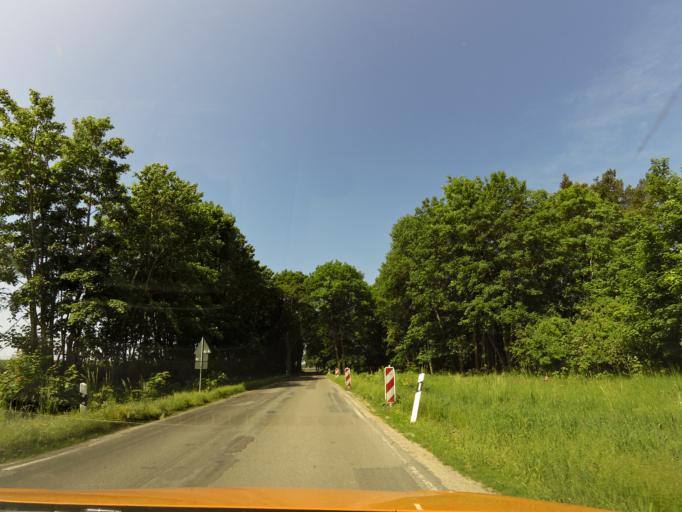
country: DE
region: Mecklenburg-Vorpommern
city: Neuburg
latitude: 53.4068
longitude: 11.9115
